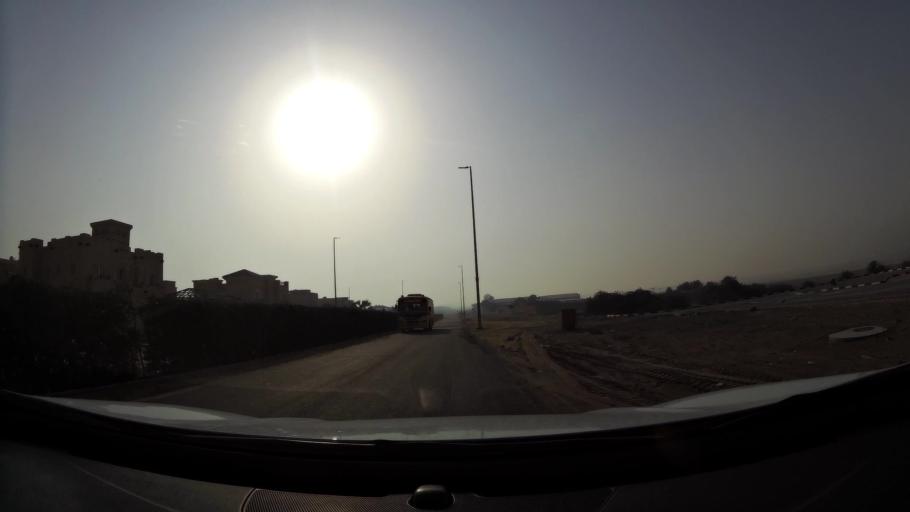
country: AE
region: Abu Dhabi
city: Abu Dhabi
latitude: 24.2941
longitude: 54.6203
